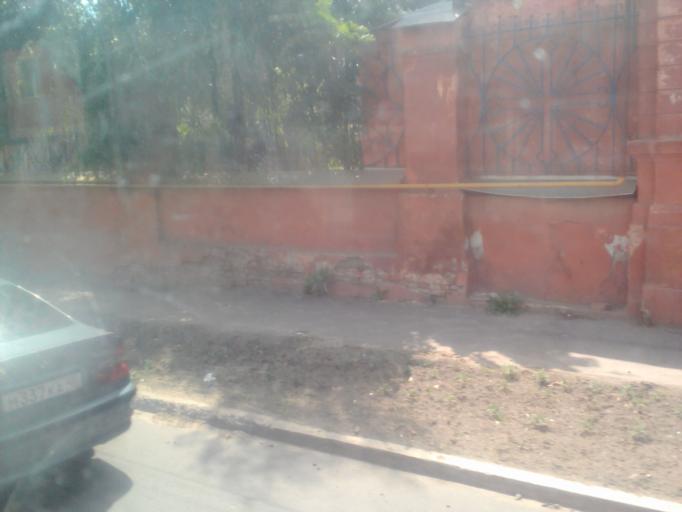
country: RU
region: Kursk
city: Kursk
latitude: 51.7322
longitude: 36.1796
